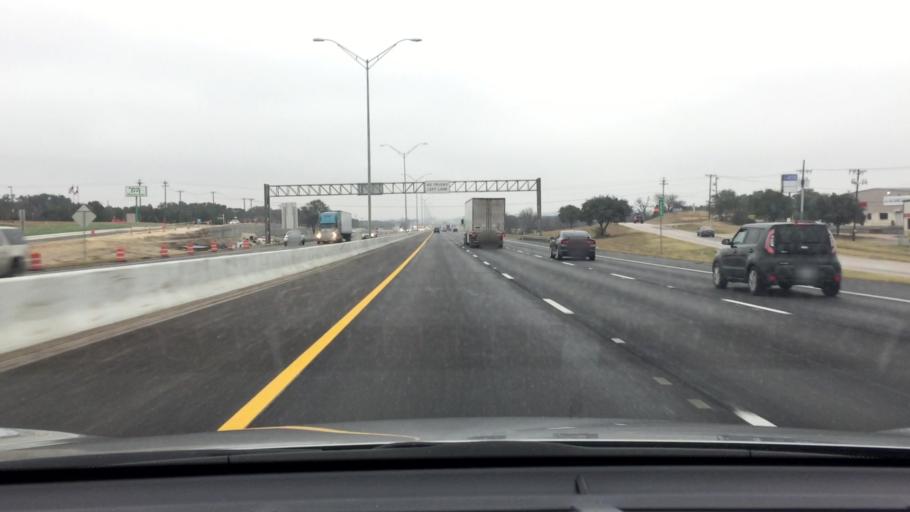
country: US
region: Texas
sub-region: Williamson County
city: Round Rock
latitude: 30.5440
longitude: -97.6923
